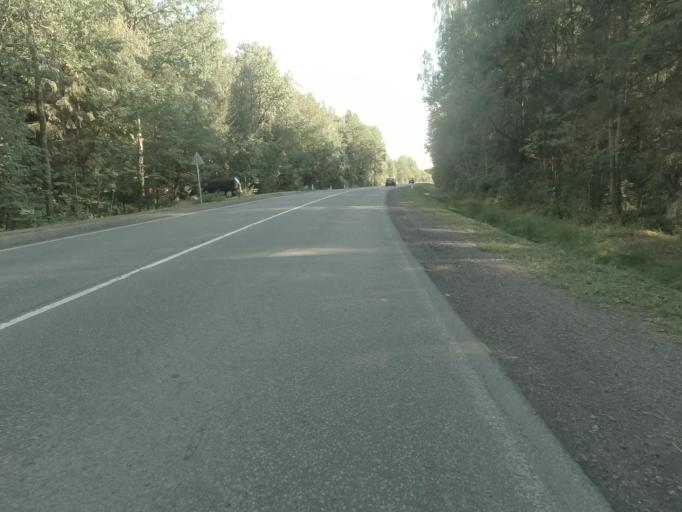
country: RU
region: Leningrad
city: Kirovsk
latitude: 59.9306
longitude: 30.9830
